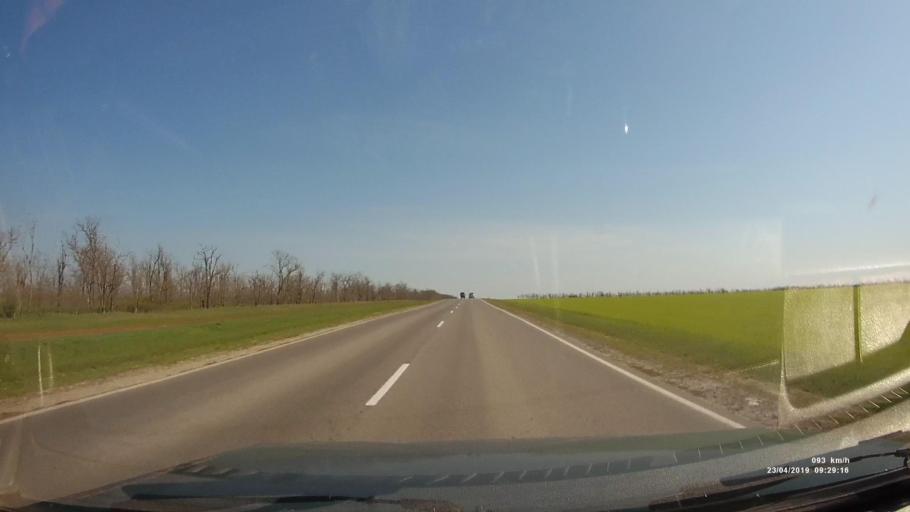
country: RU
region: Rostov
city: Proletarsk
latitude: 46.7585
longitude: 41.8026
